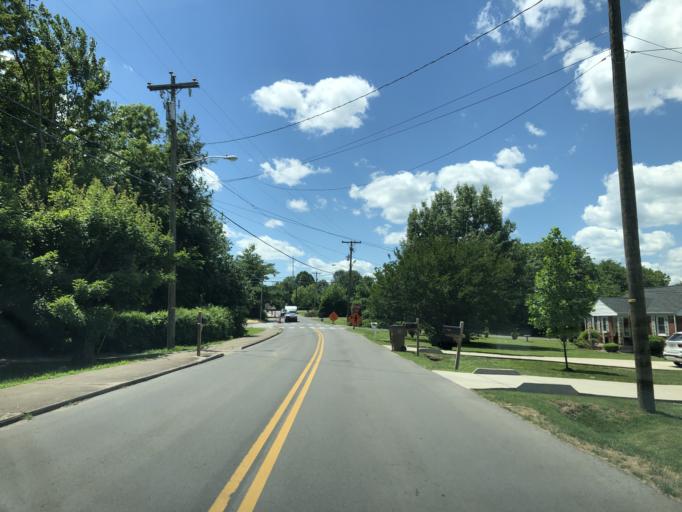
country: US
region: Tennessee
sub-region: Davidson County
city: Nashville
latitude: 36.1865
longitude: -86.7172
